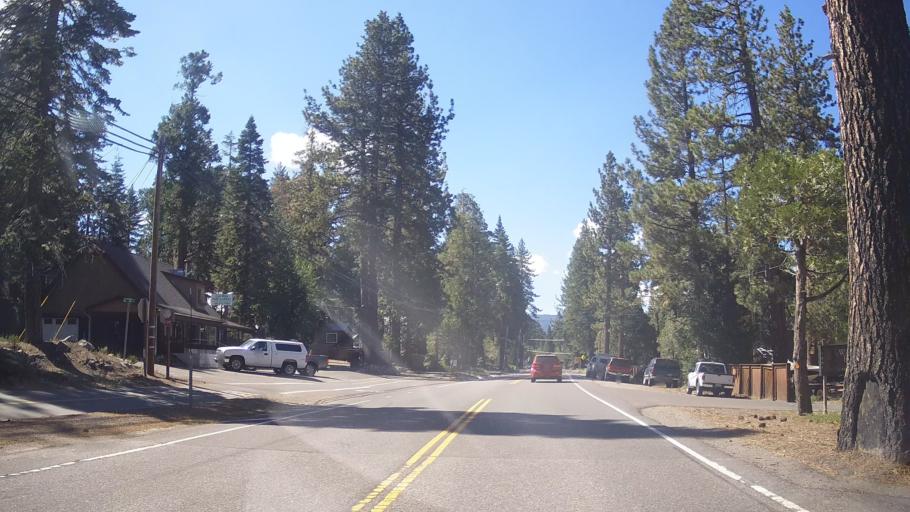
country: US
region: California
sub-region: Placer County
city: Tahoma
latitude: 39.0652
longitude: -120.1260
